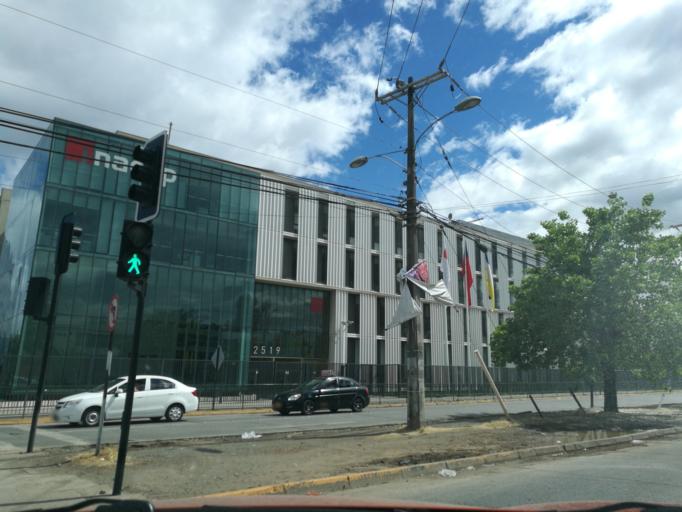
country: CL
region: O'Higgins
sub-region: Provincia de Cachapoal
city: Rancagua
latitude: -34.1368
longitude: -70.7399
